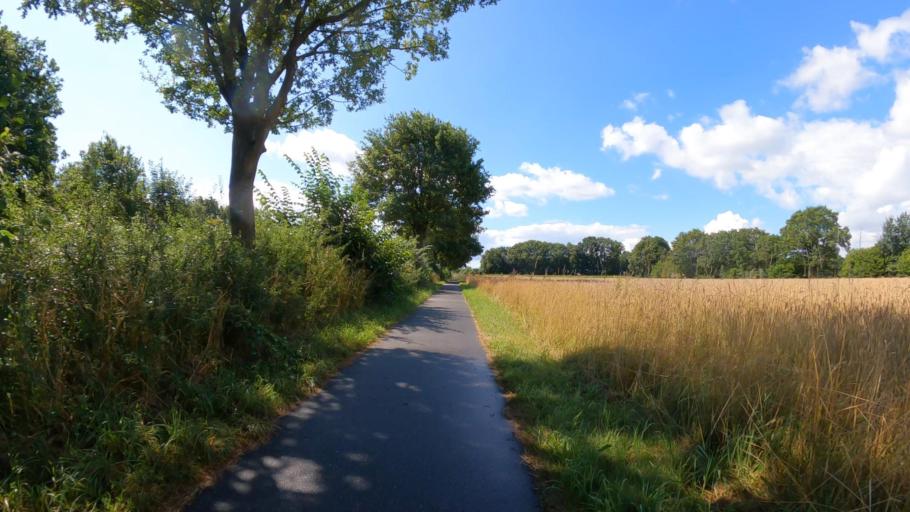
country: DE
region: Schleswig-Holstein
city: Fuhlendorf
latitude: 53.9369
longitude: 9.8932
